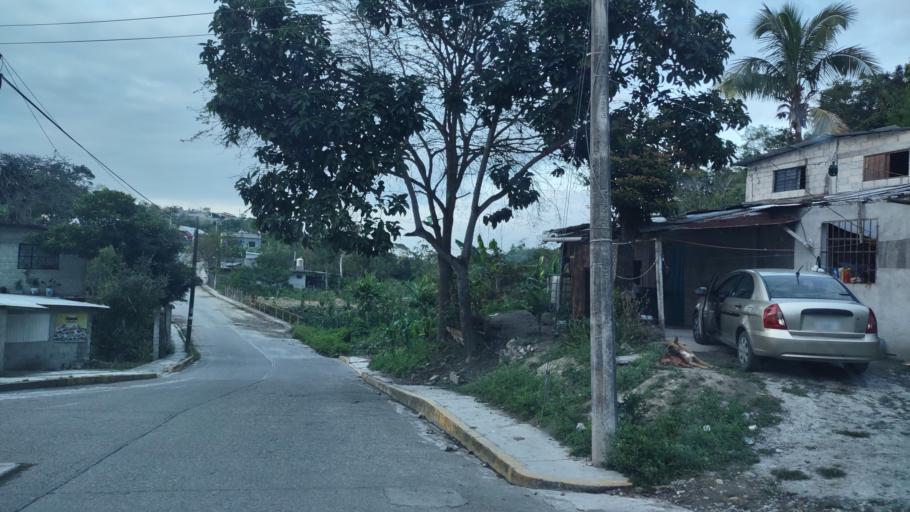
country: MX
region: Veracruz
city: Papantla de Olarte
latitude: 20.4571
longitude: -97.3064
